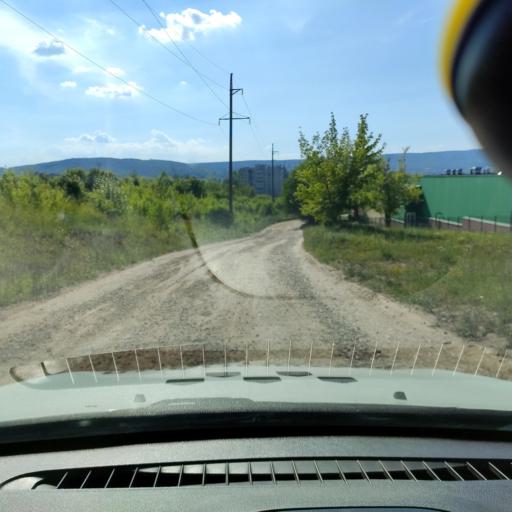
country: RU
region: Samara
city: Zhigulevsk
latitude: 53.4006
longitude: 49.5207
